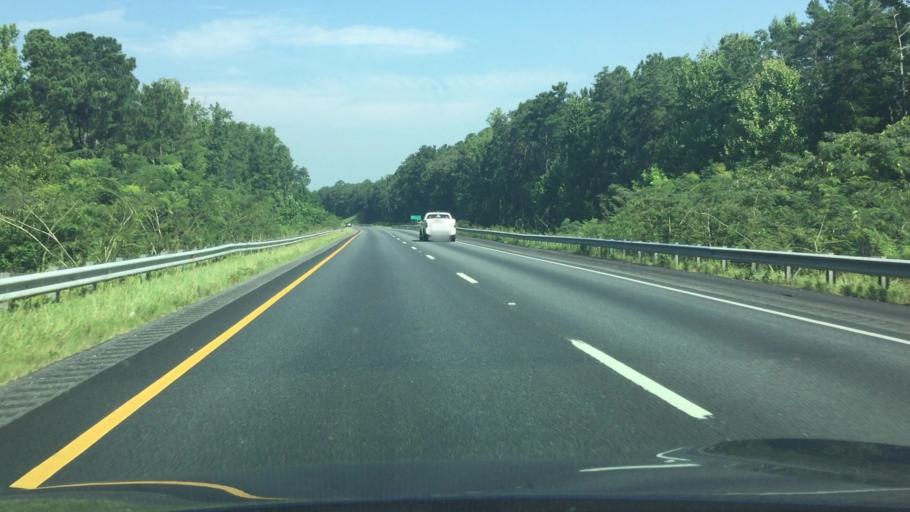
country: US
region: Alabama
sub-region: Chilton County
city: Jemison
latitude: 32.9889
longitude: -86.6937
